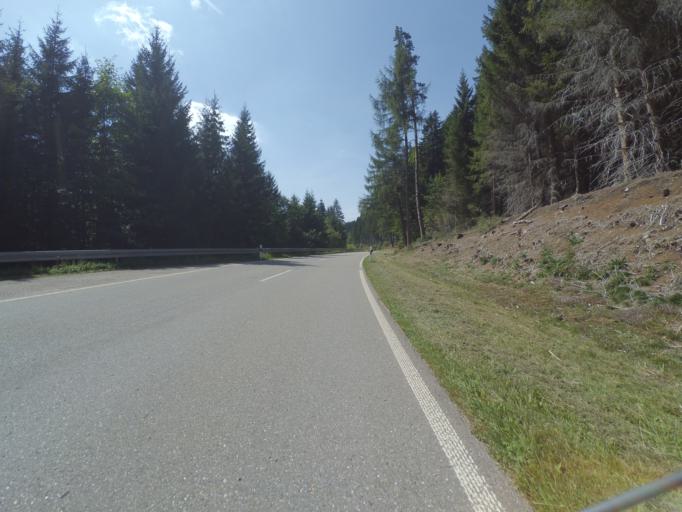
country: DE
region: Baden-Wuerttemberg
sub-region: Freiburg Region
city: Hinterzarten
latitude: 47.8817
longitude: 8.1445
